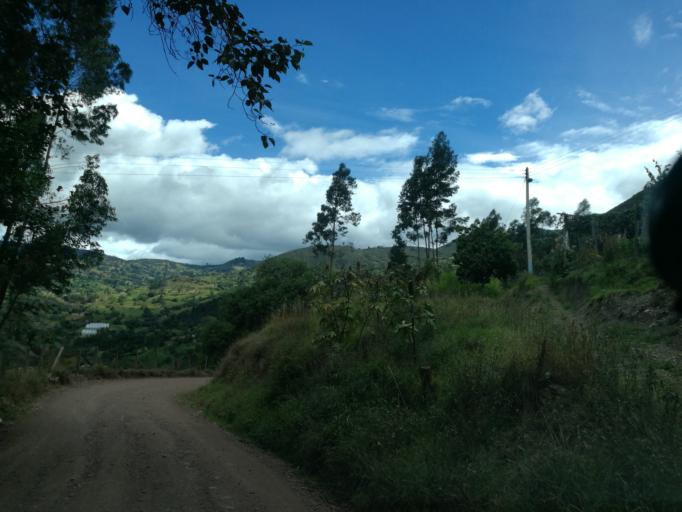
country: CO
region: Boyaca
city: Susacon
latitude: 6.1211
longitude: -72.7130
